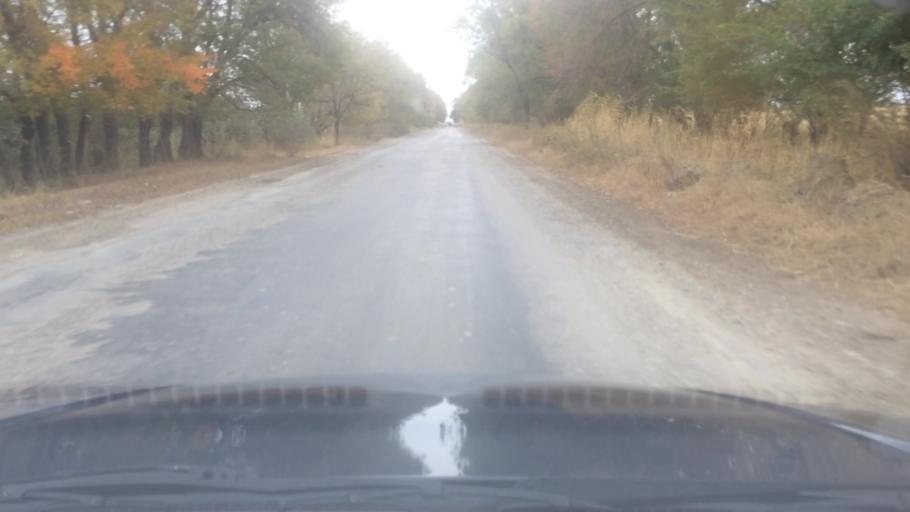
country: KG
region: Ysyk-Koel
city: Balykchy
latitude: 42.3045
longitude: 76.4752
